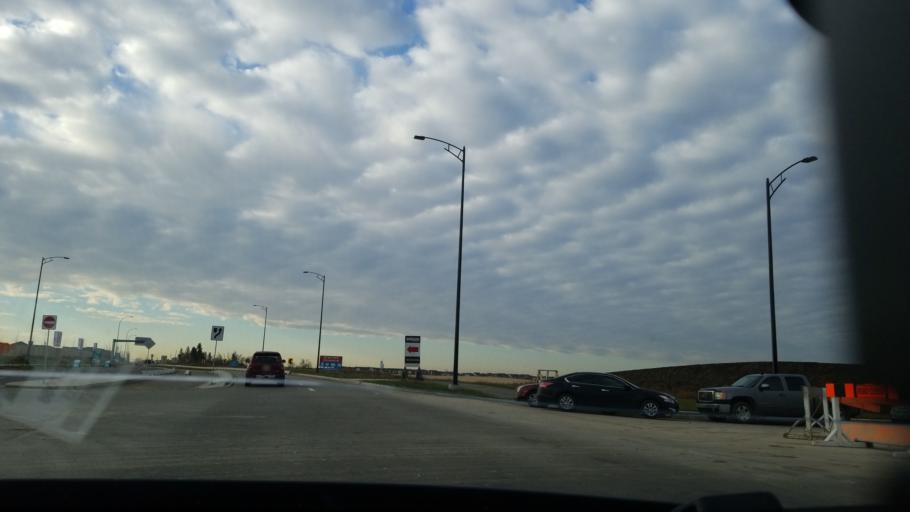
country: CA
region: Alberta
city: Edmonton
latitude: 53.6404
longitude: -113.4427
